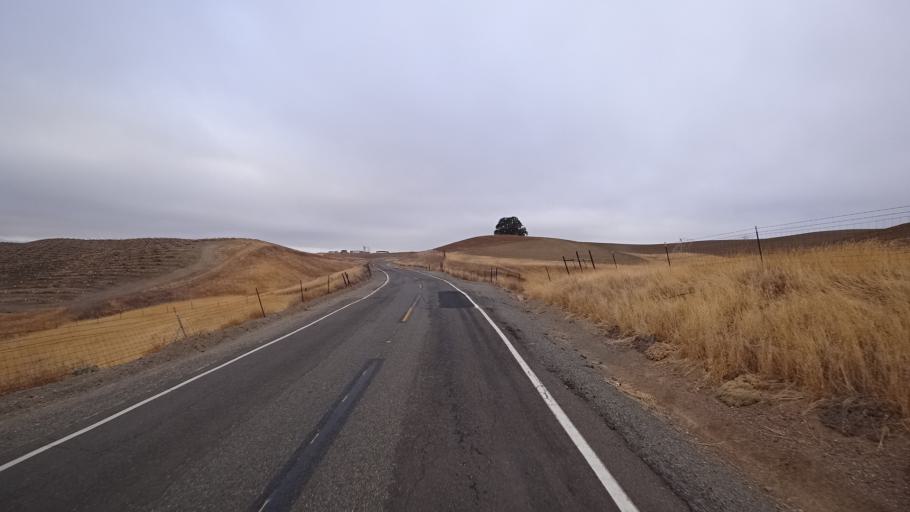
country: US
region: California
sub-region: Yolo County
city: Dunnigan
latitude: 38.8844
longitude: -122.0122
